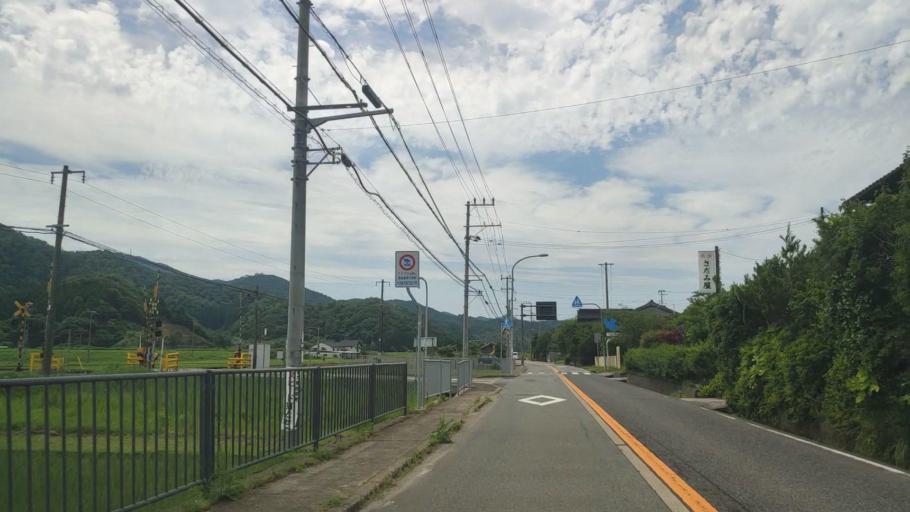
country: JP
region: Hyogo
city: Toyooka
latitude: 35.6437
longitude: 134.7581
